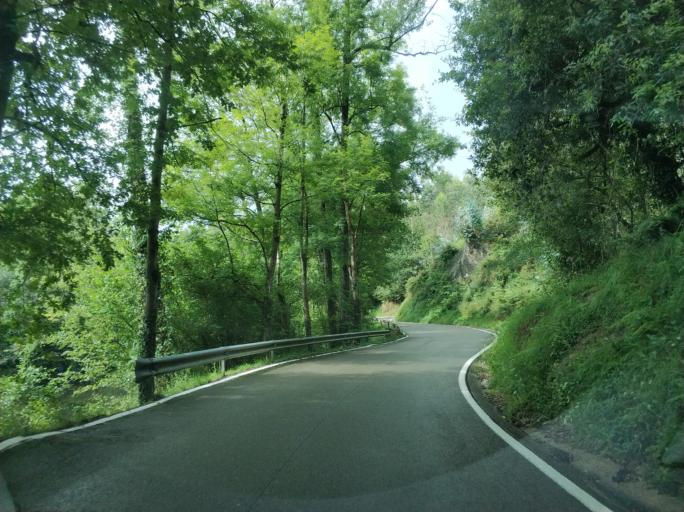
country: ES
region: Cantabria
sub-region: Provincia de Cantabria
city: Polanco
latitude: 43.3862
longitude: -3.9705
